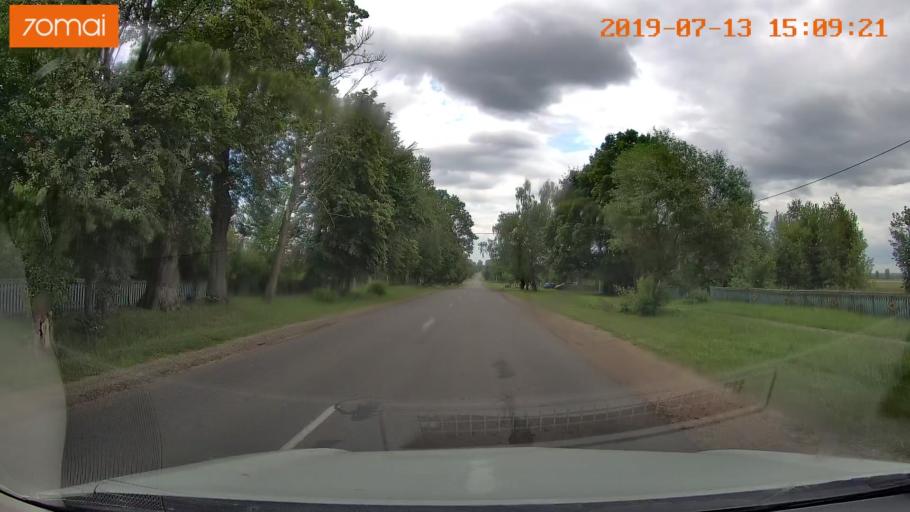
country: BY
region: Mogilev
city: Hlusha
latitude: 53.1733
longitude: 28.7605
